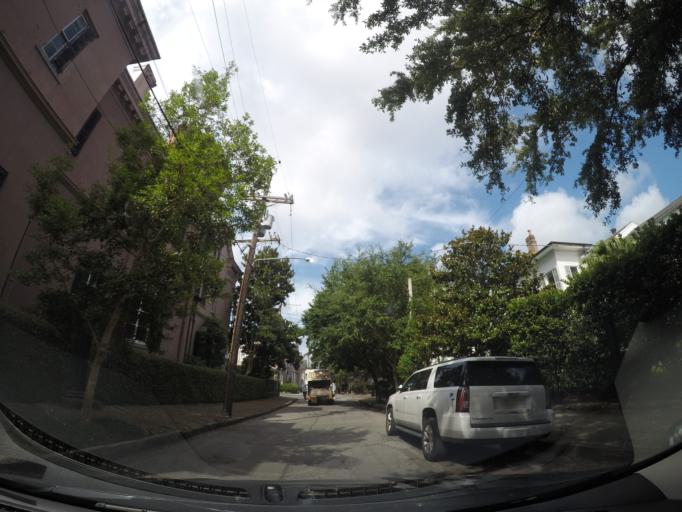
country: US
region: Louisiana
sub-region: Orleans Parish
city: New Orleans
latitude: 29.9307
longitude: -90.0805
